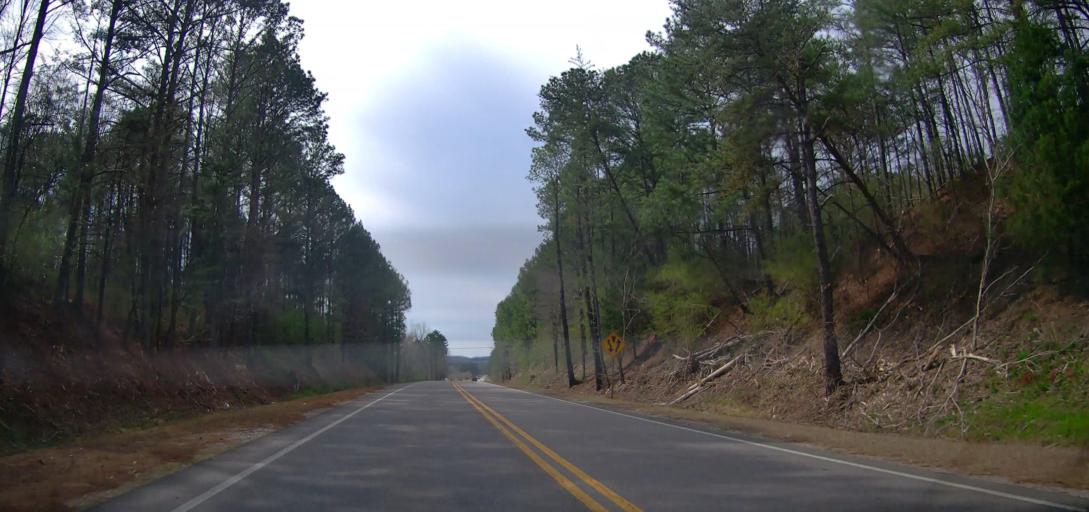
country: US
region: Alabama
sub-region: Walker County
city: Carbon Hill
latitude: 33.8765
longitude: -87.4887
